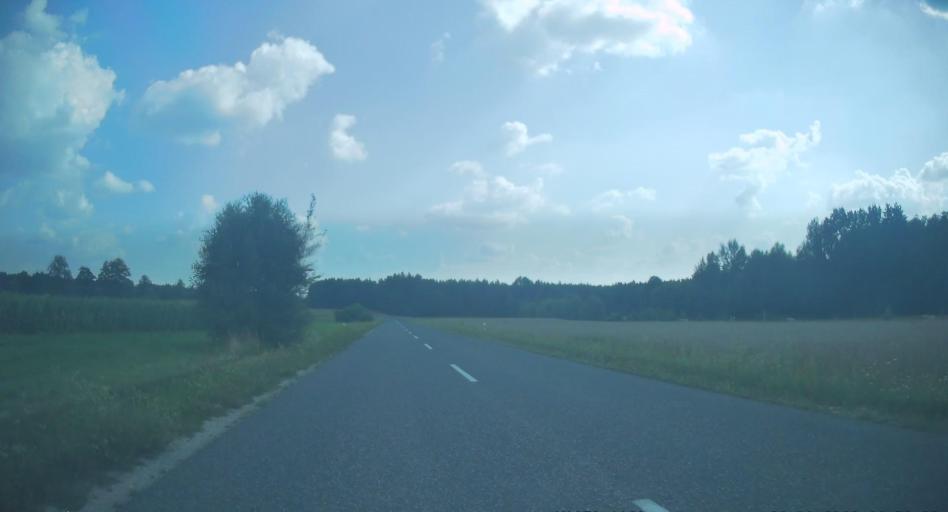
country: PL
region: Swietokrzyskie
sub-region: Powiat kielecki
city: Lopuszno
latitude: 50.9033
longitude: 20.2473
